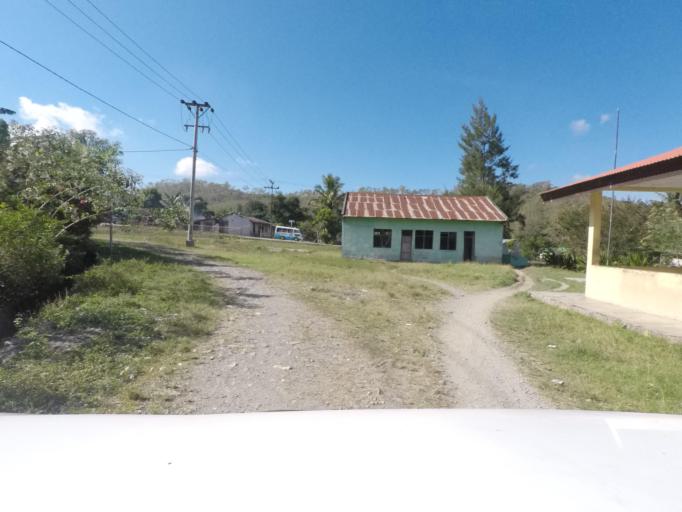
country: TL
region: Ermera
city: Gleno
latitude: -8.7116
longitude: 125.4539
